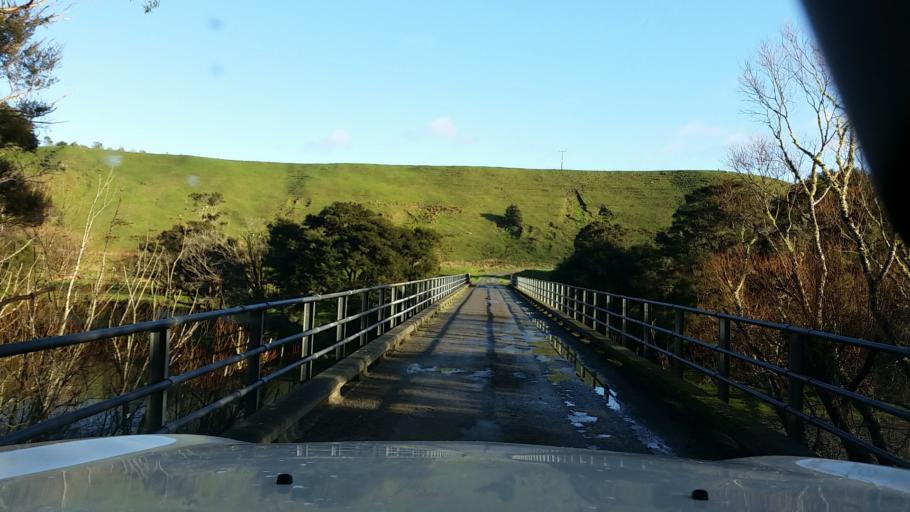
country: NZ
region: Wellington
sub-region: South Wairarapa District
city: Waipawa
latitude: -41.2670
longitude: 175.6881
